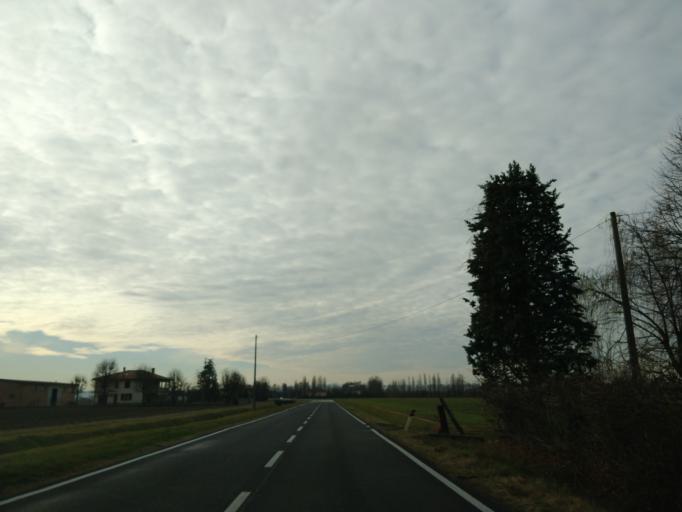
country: IT
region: Emilia-Romagna
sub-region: Provincia di Bologna
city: Argelato
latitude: 44.6272
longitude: 11.3394
